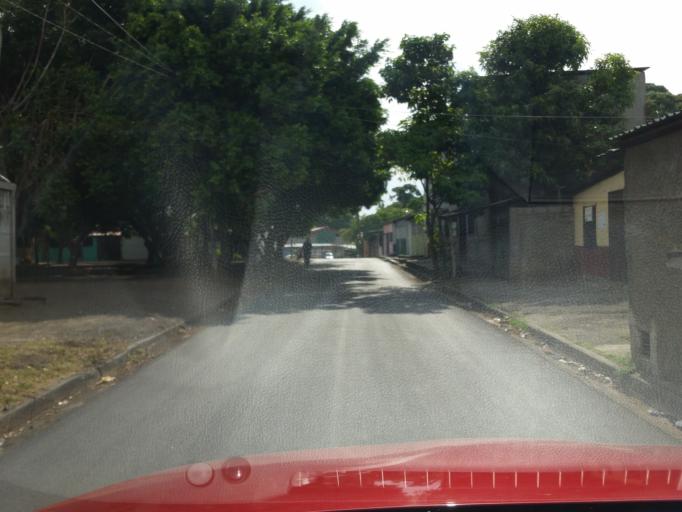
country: NI
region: Managua
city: Managua
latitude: 12.1263
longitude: -86.2498
